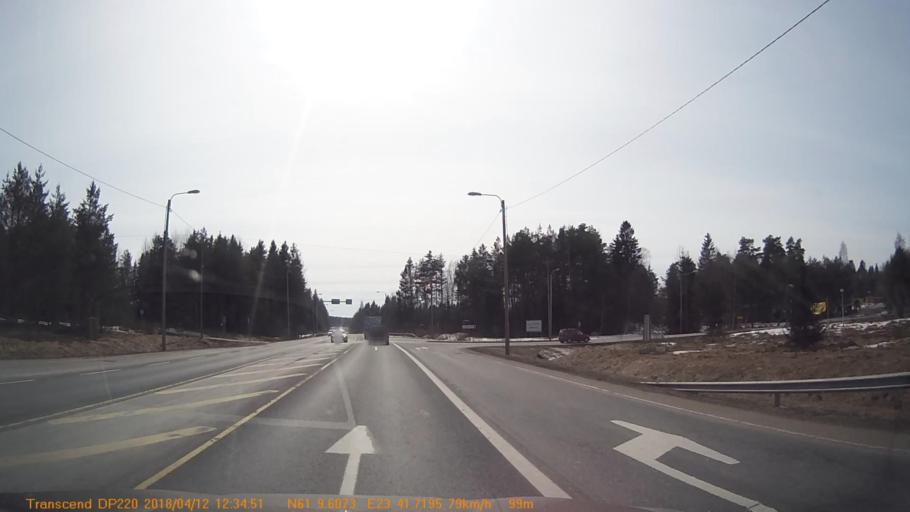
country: FI
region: Pirkanmaa
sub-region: Etelae-Pirkanmaa
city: Kylmaekoski
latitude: 61.1603
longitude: 23.6954
